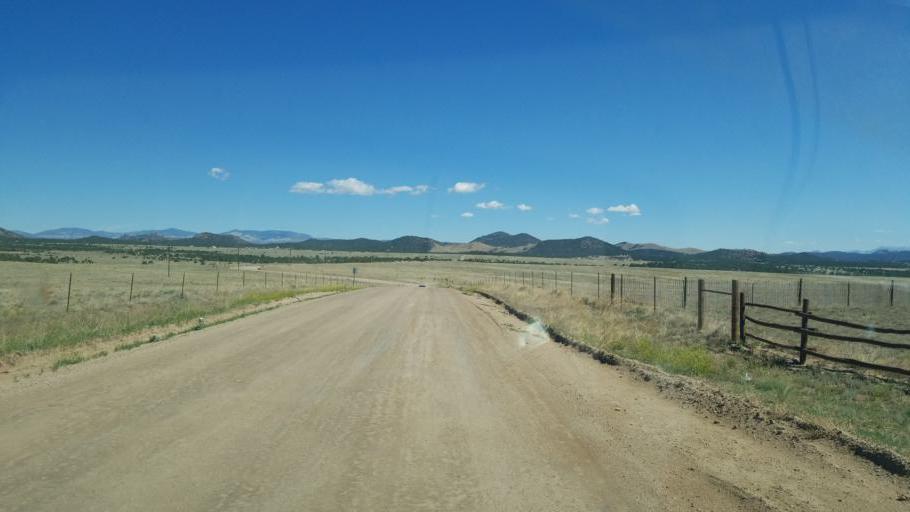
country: US
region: Colorado
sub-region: Custer County
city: Westcliffe
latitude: 38.2597
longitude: -105.4998
